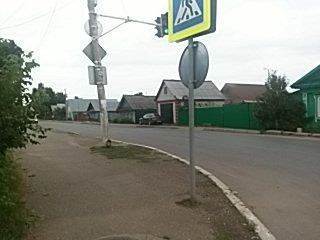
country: RU
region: Tatarstan
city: Yelabuga
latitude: 55.7550
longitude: 52.0819
